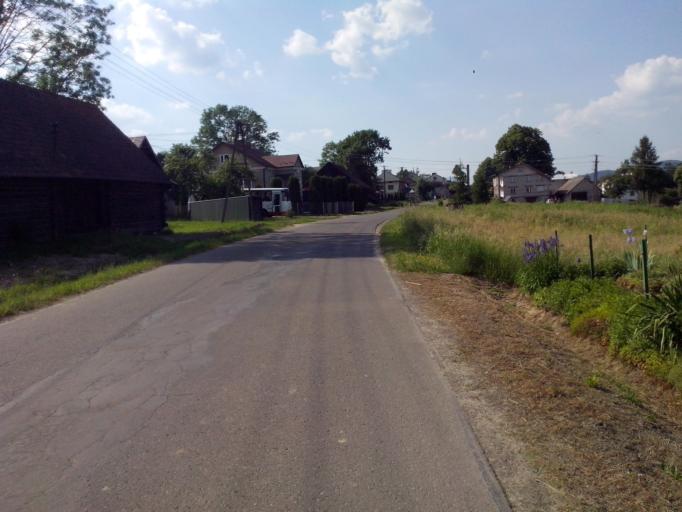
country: PL
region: Subcarpathian Voivodeship
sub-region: Powiat brzozowski
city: Stara Wies
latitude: 49.7304
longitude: 21.9868
